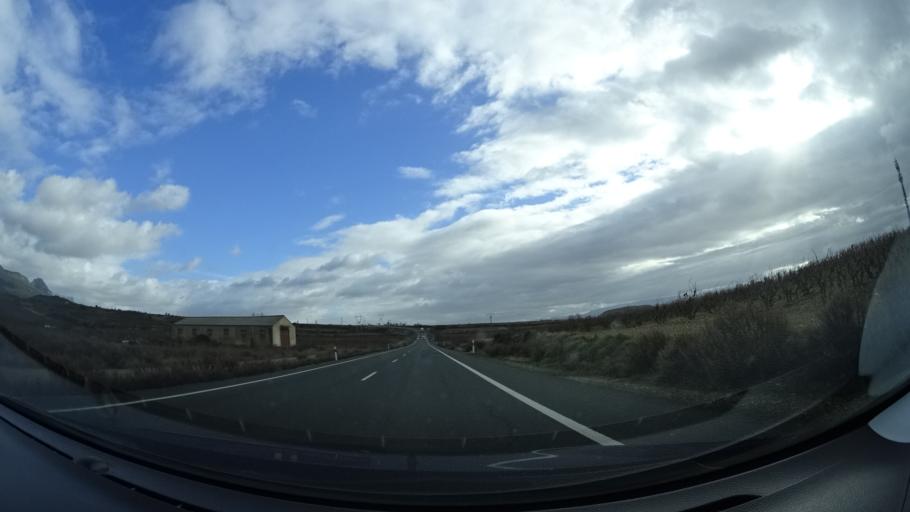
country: ES
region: La Rioja
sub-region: Provincia de La Rioja
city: San Vicente de la Sonsierra
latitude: 42.5697
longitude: -2.7511
